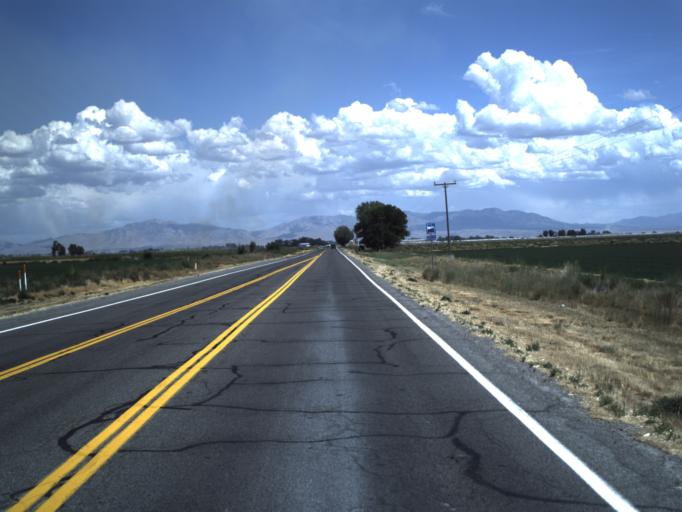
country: US
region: Utah
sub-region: Millard County
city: Delta
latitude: 39.3307
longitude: -112.6502
